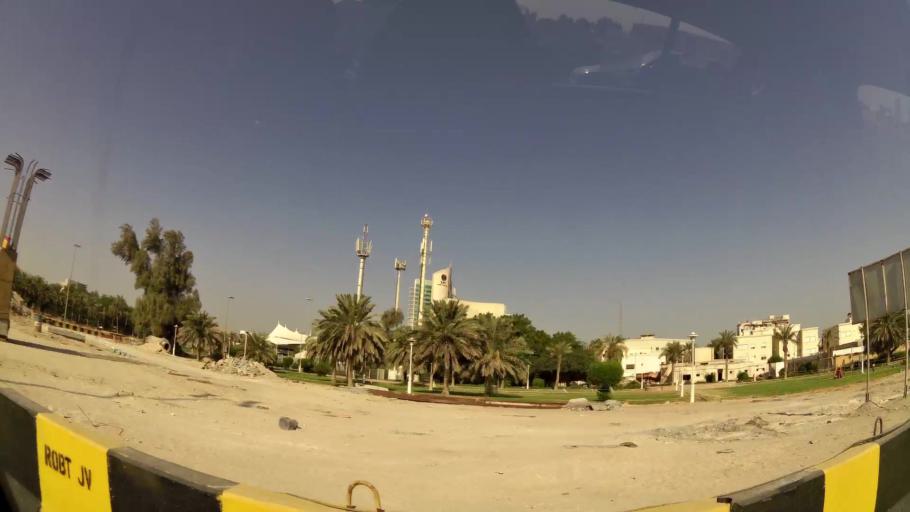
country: KW
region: Al Asimah
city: Ash Shamiyah
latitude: 29.3523
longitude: 47.9457
